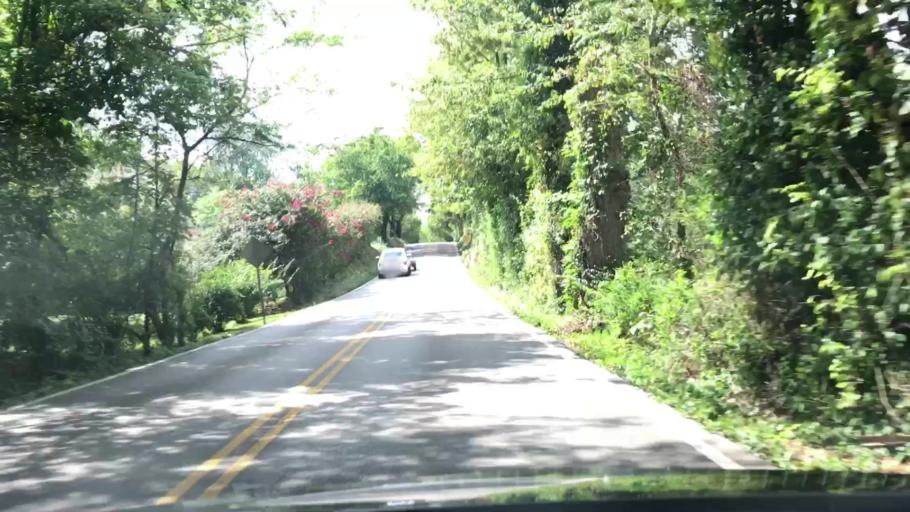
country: US
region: Tennessee
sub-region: Williamson County
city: Thompson's Station
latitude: 35.7802
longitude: -86.8803
